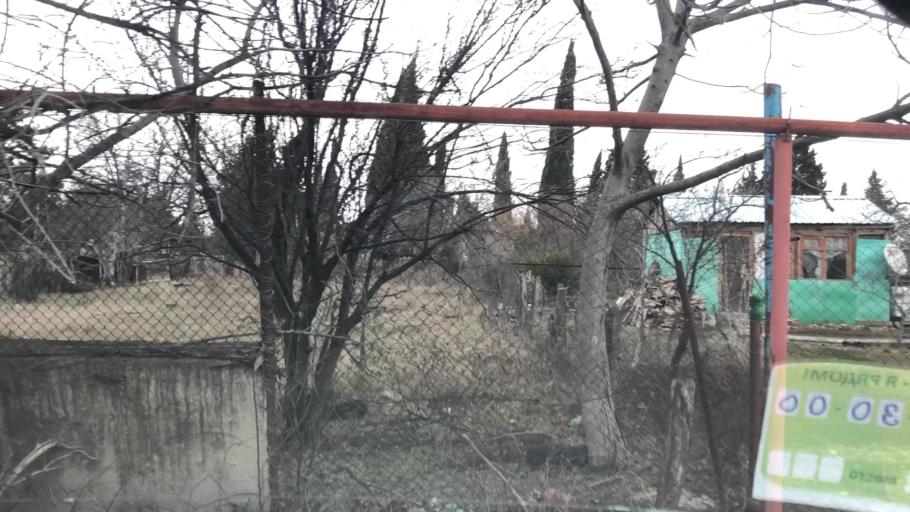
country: GE
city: Didi Lilo
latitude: 41.7014
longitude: 44.9247
